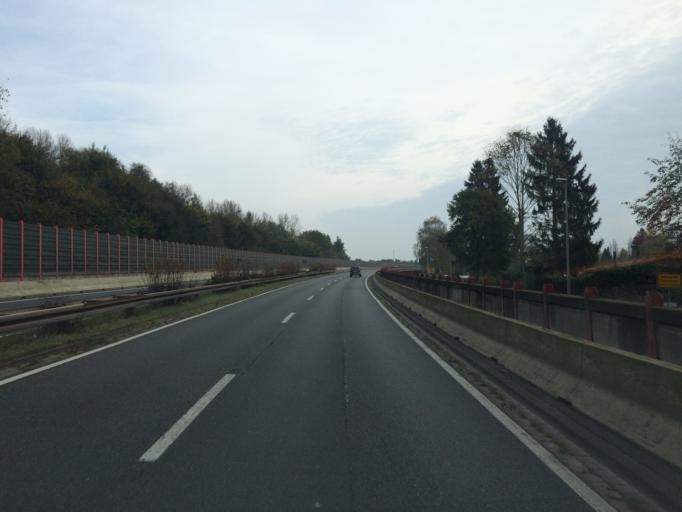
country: DE
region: Lower Saxony
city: Hannover
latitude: 52.3916
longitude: 9.7887
